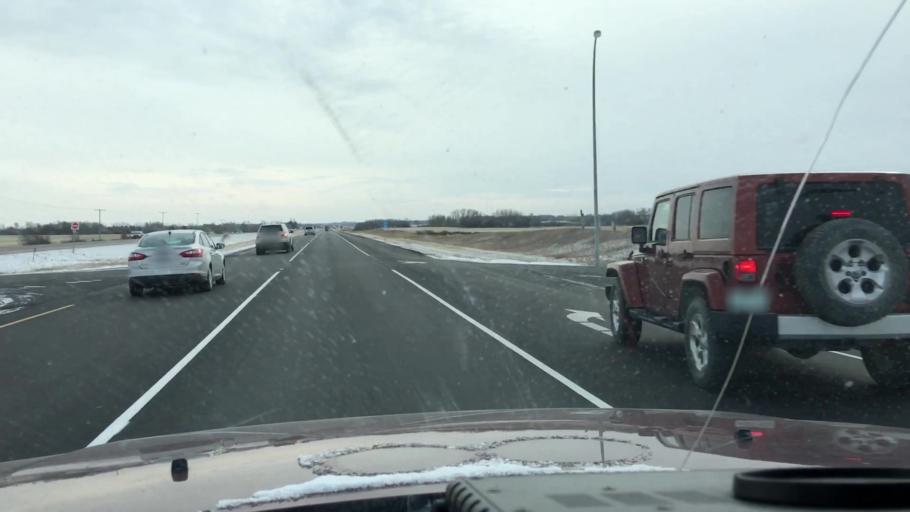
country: CA
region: Saskatchewan
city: Saskatoon
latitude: 52.0274
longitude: -106.5822
